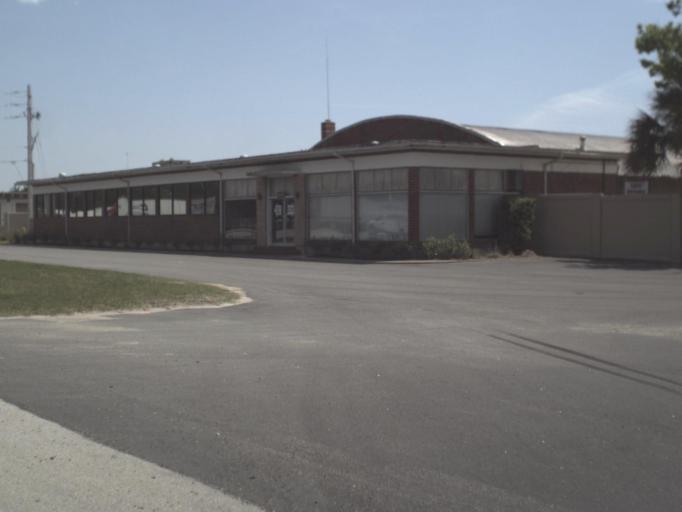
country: US
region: Florida
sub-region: Duval County
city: Jacksonville
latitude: 30.2745
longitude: -81.6244
